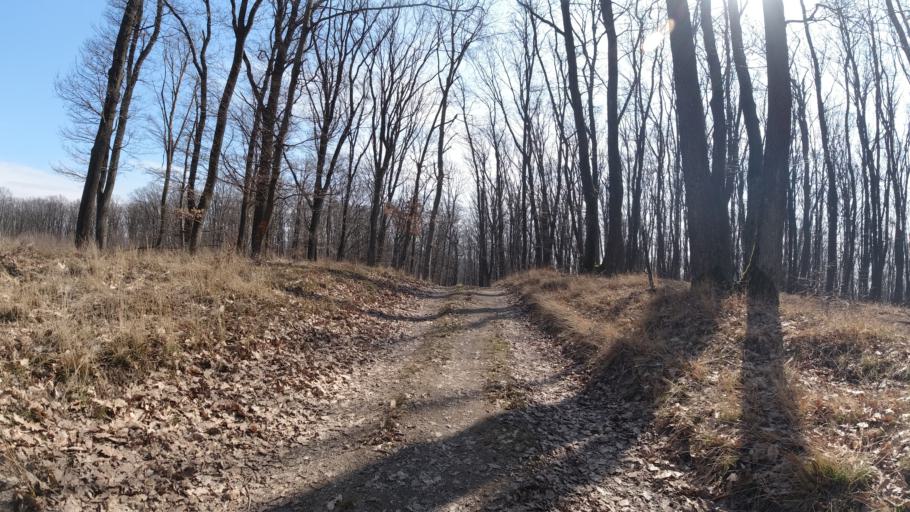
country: SK
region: Trnavsky
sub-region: Okres Trnava
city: Piestany
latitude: 48.5906
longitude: 17.9061
